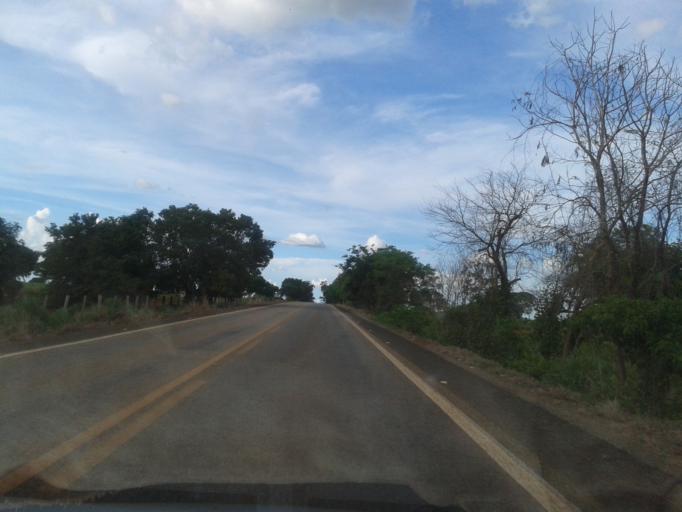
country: BR
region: Goias
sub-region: Crixas
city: Crixas
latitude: -14.0792
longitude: -50.3331
